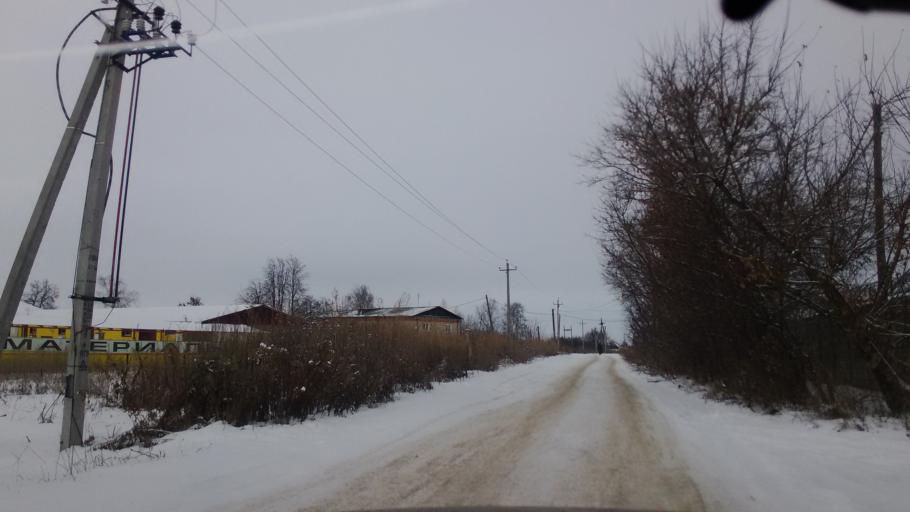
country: RU
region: Tula
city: Bogoroditsk
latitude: 53.7640
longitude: 38.1026
